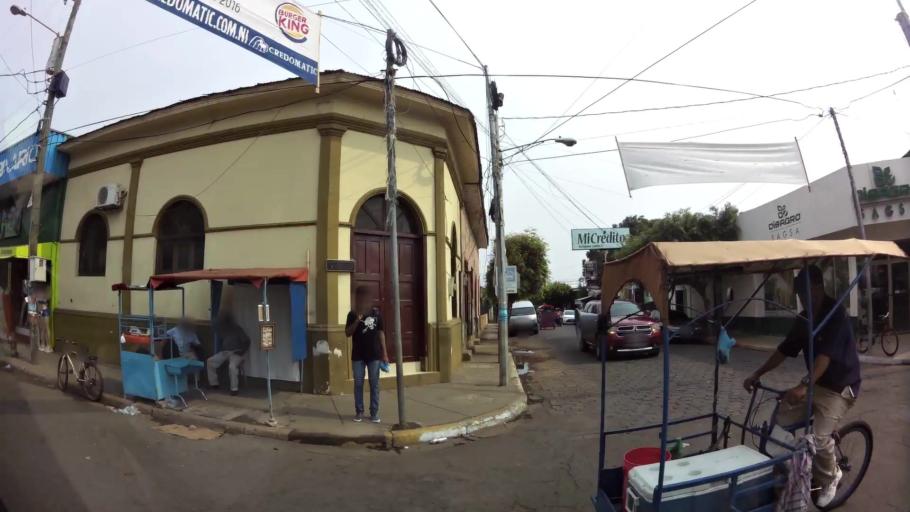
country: NI
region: Chinandega
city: Chinandega
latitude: 12.6307
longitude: -87.1342
